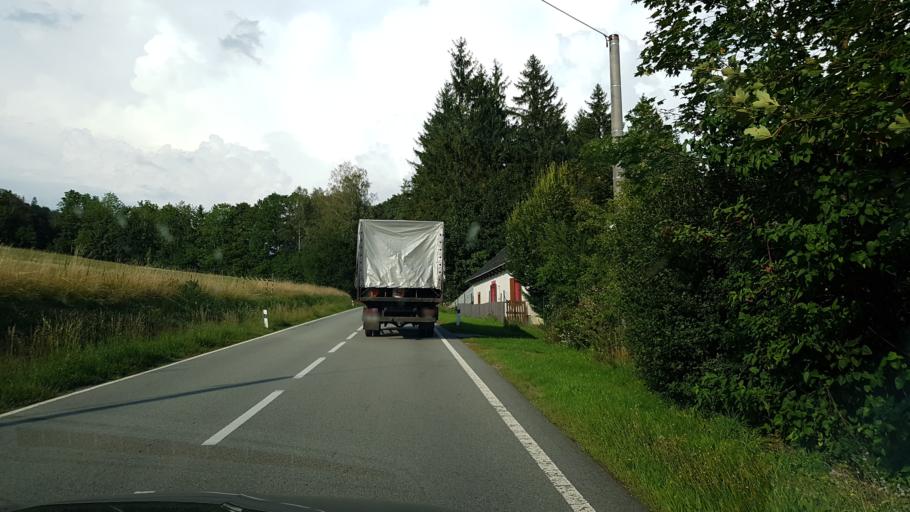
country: CZ
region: Pardubicky
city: Jablonne nad Orlici
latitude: 50.0901
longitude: 16.6052
